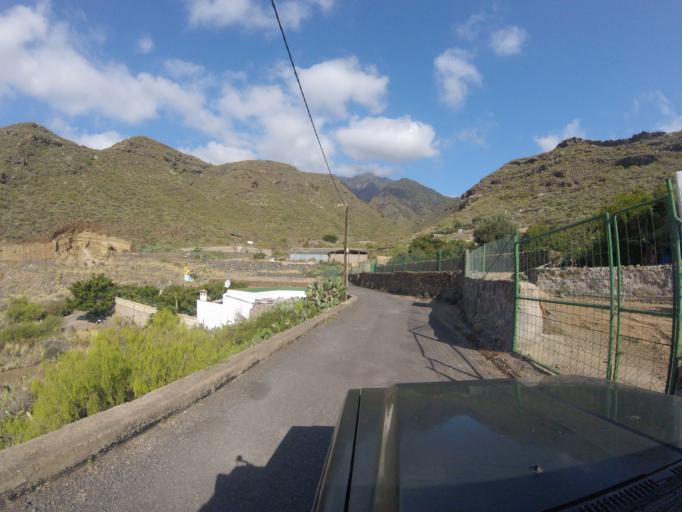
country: ES
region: Canary Islands
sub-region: Provincia de Santa Cruz de Tenerife
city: Candelaria
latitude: 28.3787
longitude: -16.3759
